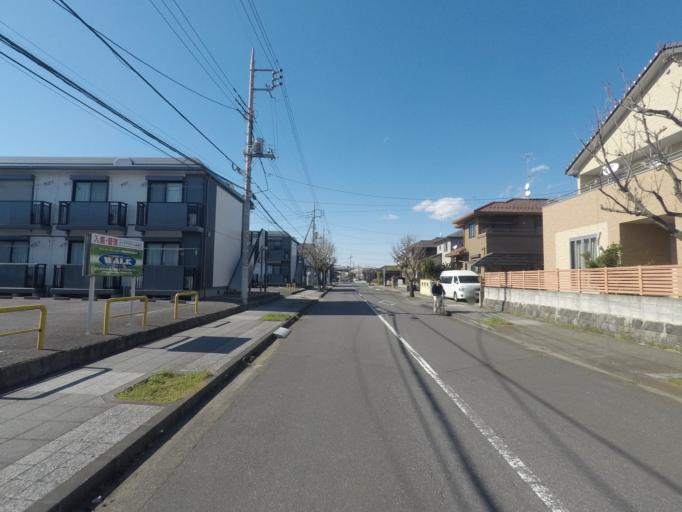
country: JP
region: Ibaraki
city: Naka
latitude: 36.1124
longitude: 140.1102
